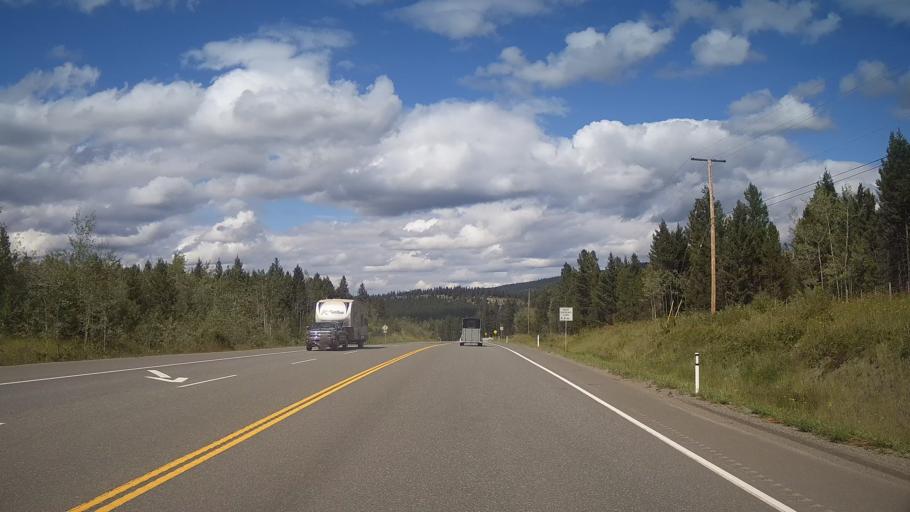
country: CA
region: British Columbia
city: Williams Lake
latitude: 51.7413
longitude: -121.3312
